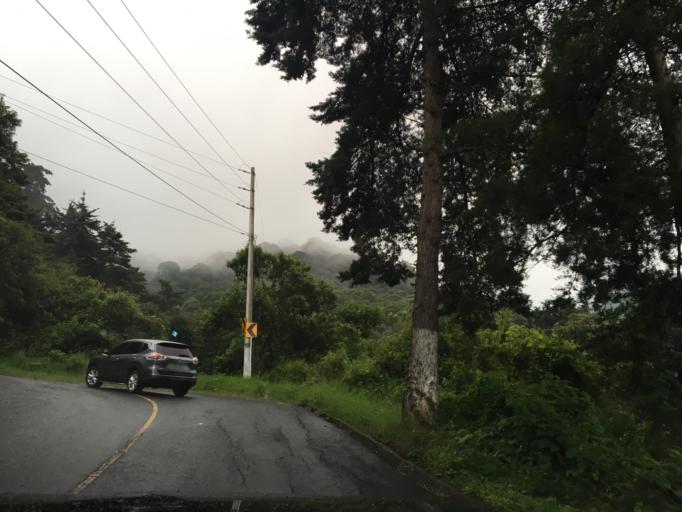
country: GT
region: Guatemala
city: Santa Catarina Pinula
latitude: 14.5464
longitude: -90.4989
